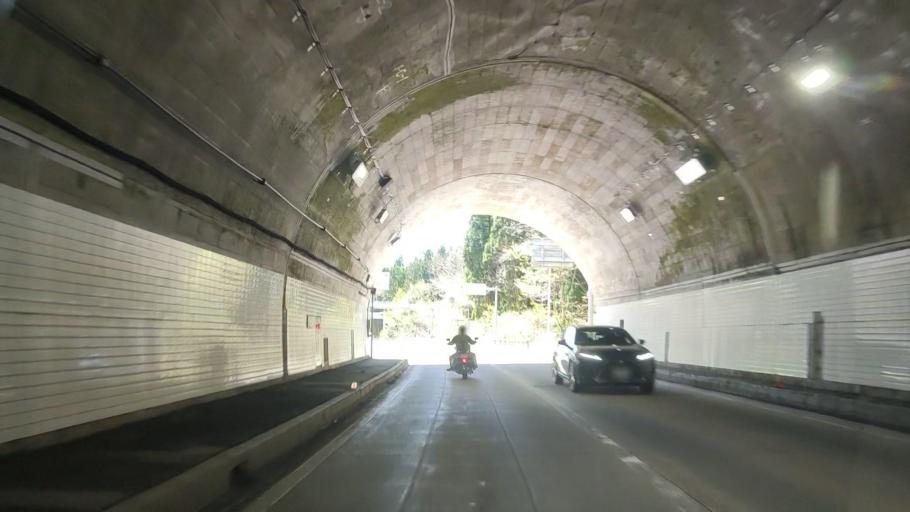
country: JP
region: Akita
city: Yuzawa
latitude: 39.0006
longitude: 140.3649
